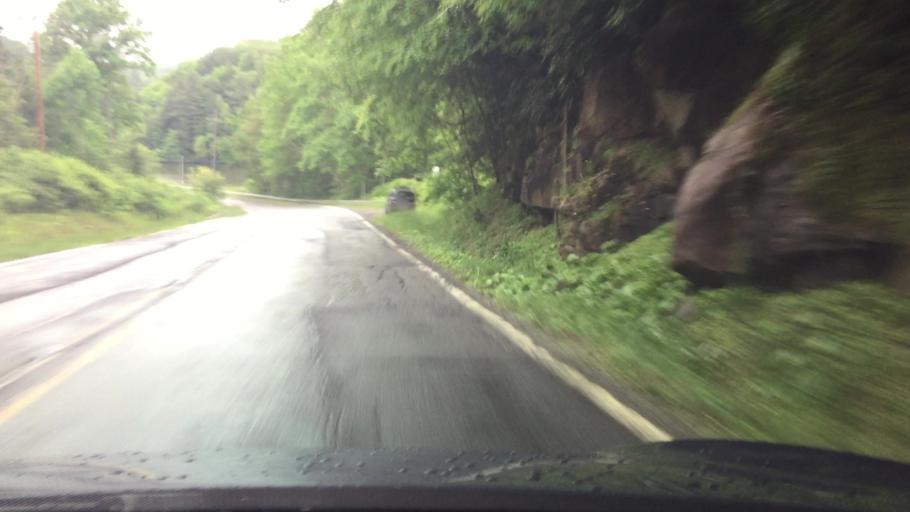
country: US
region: West Virginia
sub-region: Raleigh County
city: Shady Spring
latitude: 37.6861
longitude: -81.0555
